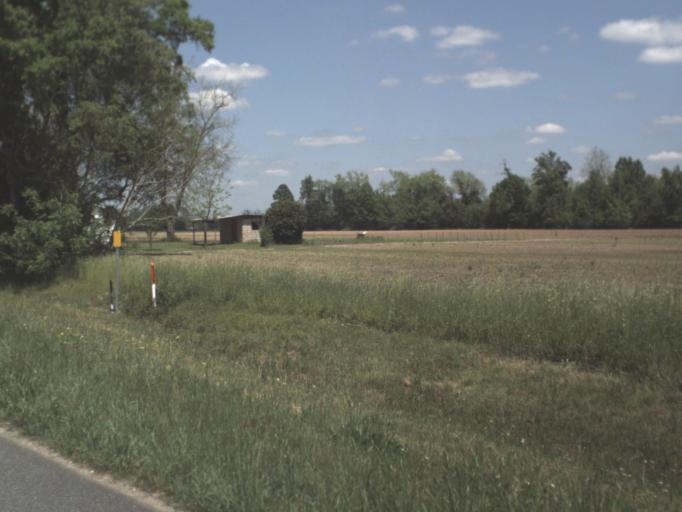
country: US
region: Alabama
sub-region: Escambia County
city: East Brewton
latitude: 30.9798
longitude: -87.0442
